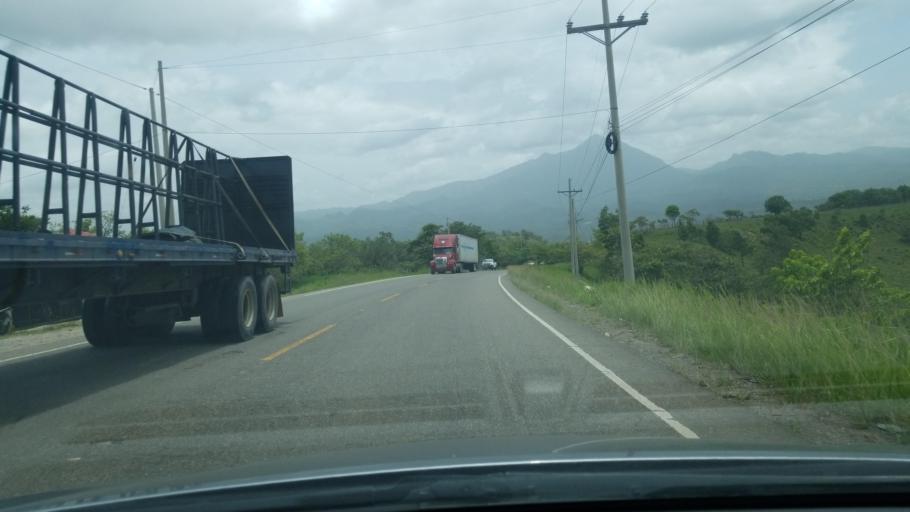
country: HN
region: Copan
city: Cucuyagua
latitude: 14.6695
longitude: -88.8495
